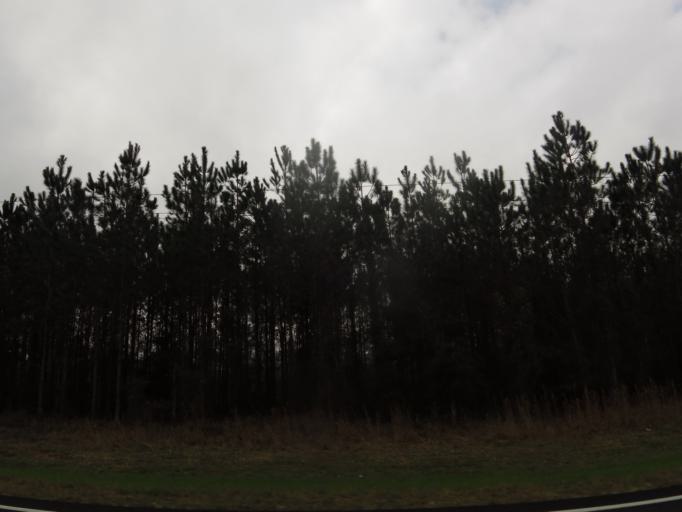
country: US
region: Florida
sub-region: Gilchrist County
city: Trenton
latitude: 29.7885
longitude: -82.7932
